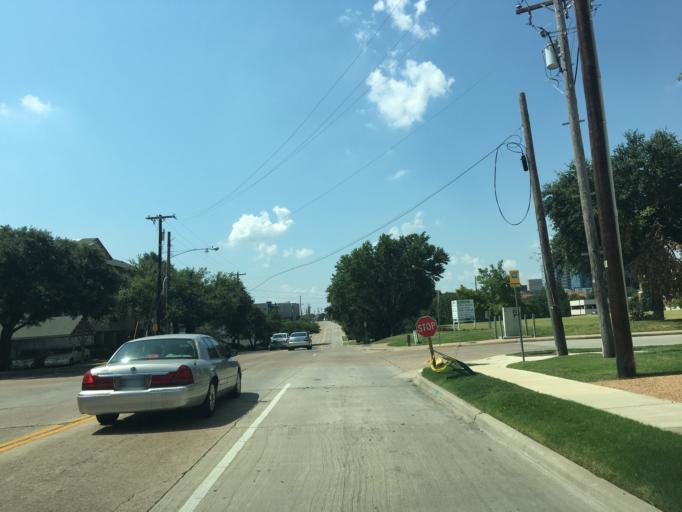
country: US
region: Texas
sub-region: Dallas County
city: Addison
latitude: 32.9654
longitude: -96.8190
